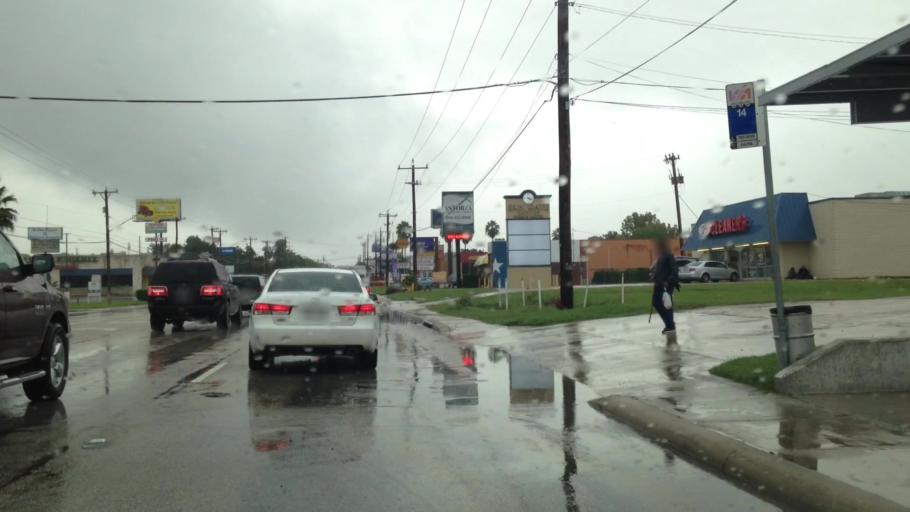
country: US
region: Texas
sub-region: Bexar County
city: Windcrest
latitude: 29.5239
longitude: -98.4110
